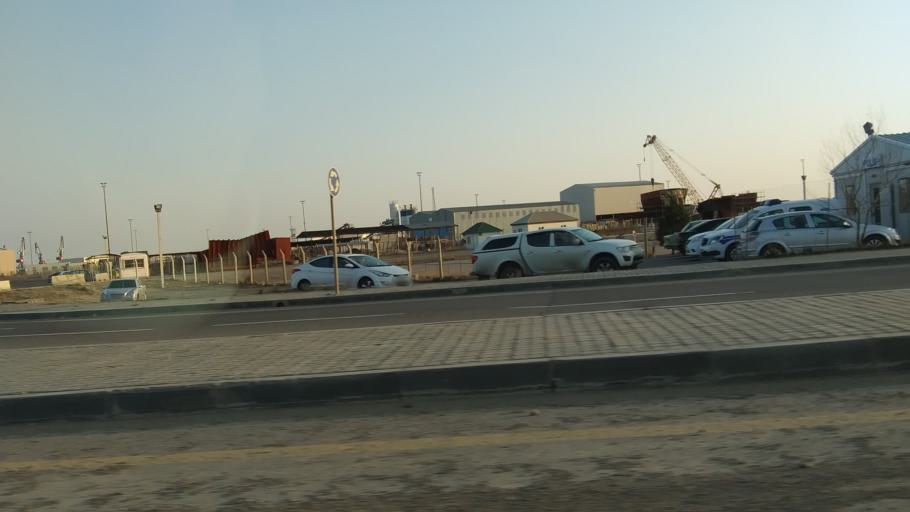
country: AZ
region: Baki
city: Qobustan
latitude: 39.9813
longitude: 49.4391
